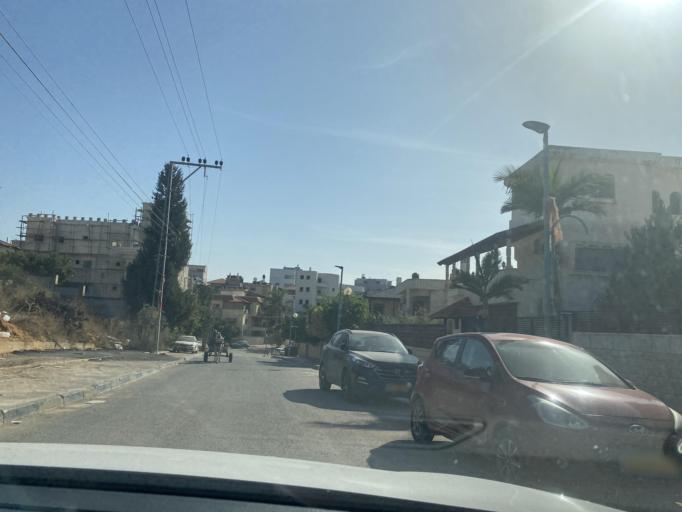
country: IL
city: Oranit
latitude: 32.1320
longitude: 34.9747
